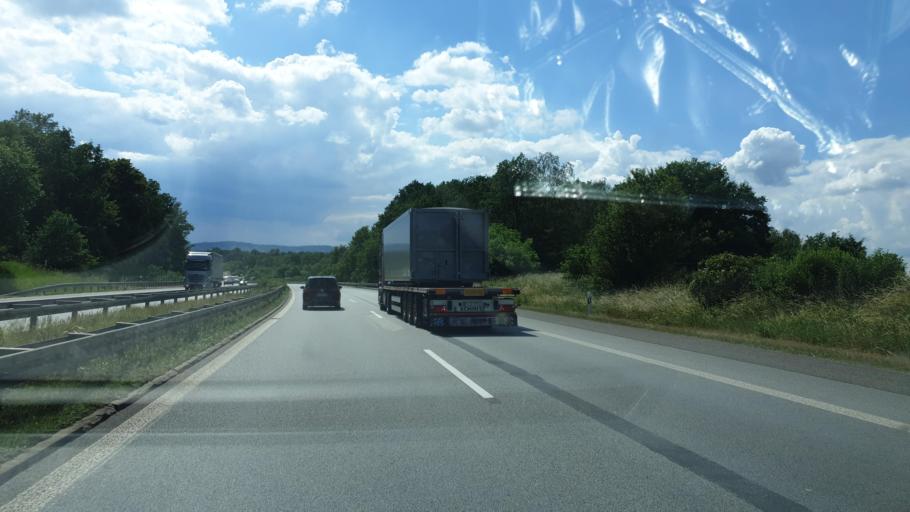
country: DE
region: Saxony
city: Burkau
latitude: 51.1977
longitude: 14.2117
